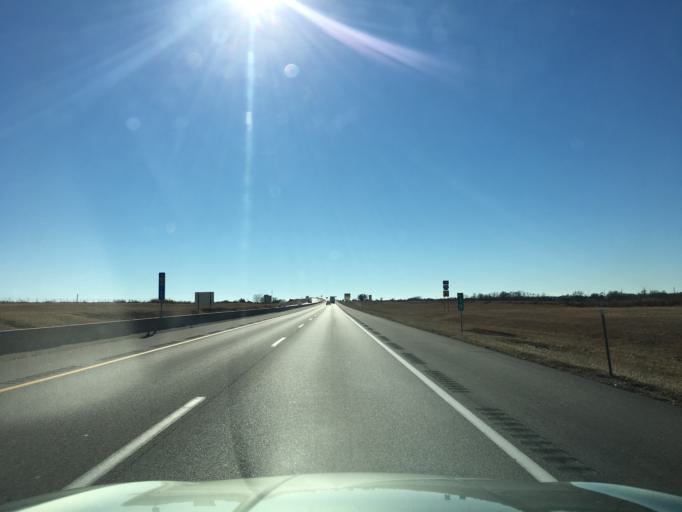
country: US
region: Kansas
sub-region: Sumner County
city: Wellington
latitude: 37.2740
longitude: -97.3404
